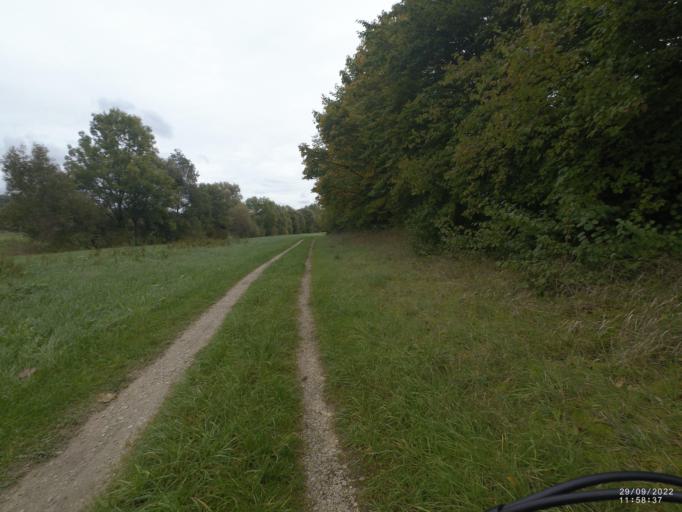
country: DE
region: Baden-Wuerttemberg
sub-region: Regierungsbezirk Stuttgart
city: Ebersbach an der Fils
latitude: 48.7118
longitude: 9.5001
